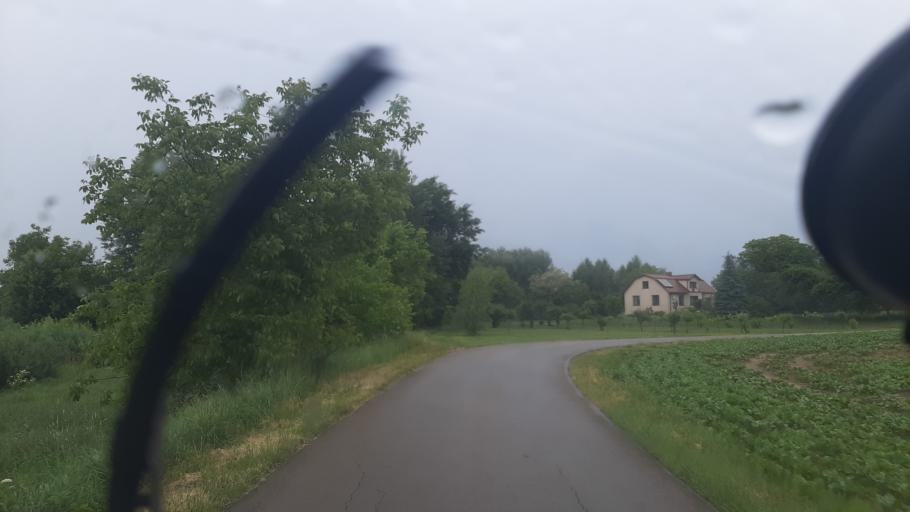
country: PL
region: Lublin Voivodeship
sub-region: Powiat lubelski
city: Garbow
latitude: 51.3537
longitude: 22.3438
